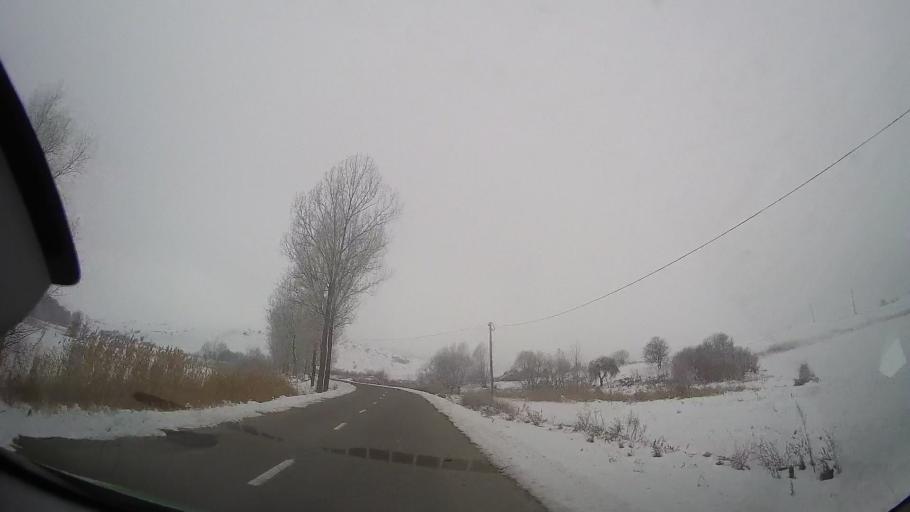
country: RO
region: Neamt
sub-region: Comuna Oniceni
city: Oniceni
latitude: 46.8020
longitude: 27.1320
